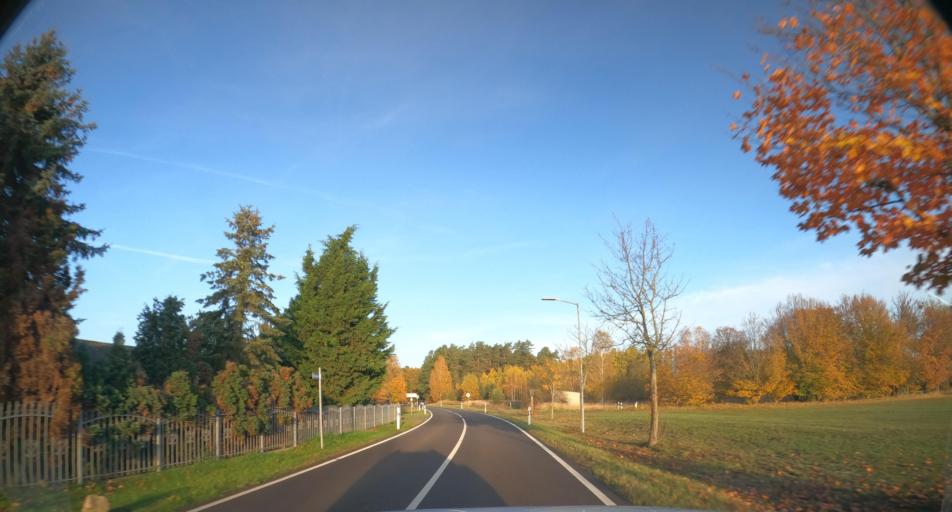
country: DE
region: Mecklenburg-Vorpommern
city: Ahlbeck
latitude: 53.6470
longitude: 14.1948
